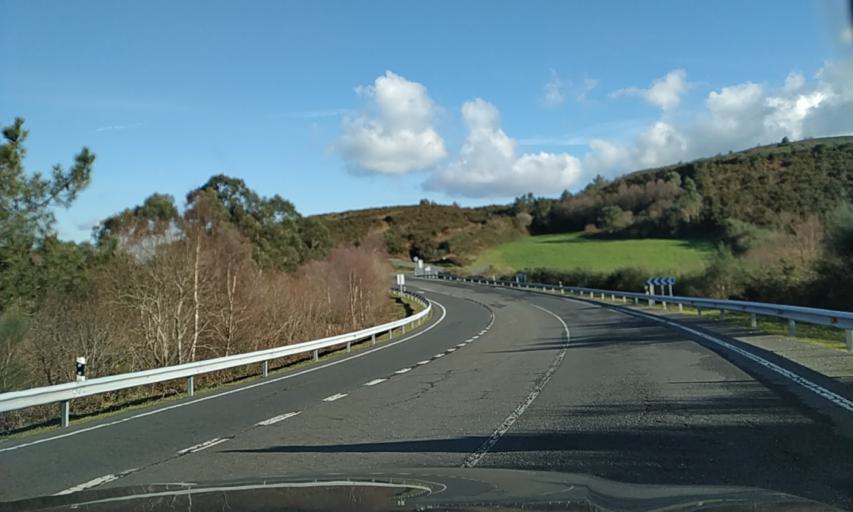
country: ES
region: Galicia
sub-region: Provincia de Pontevedra
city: Silleda
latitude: 42.6986
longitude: -8.3381
